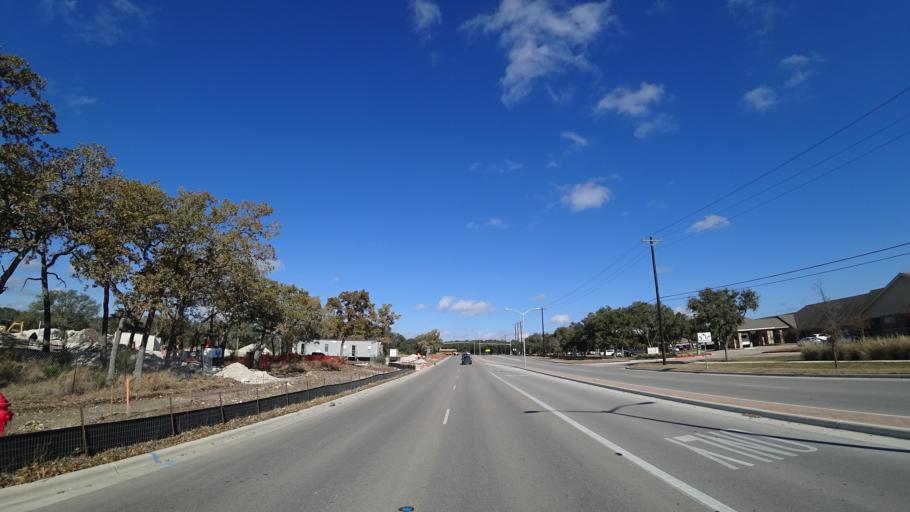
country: US
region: Texas
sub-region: Williamson County
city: Cedar Park
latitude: 30.5349
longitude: -97.8085
